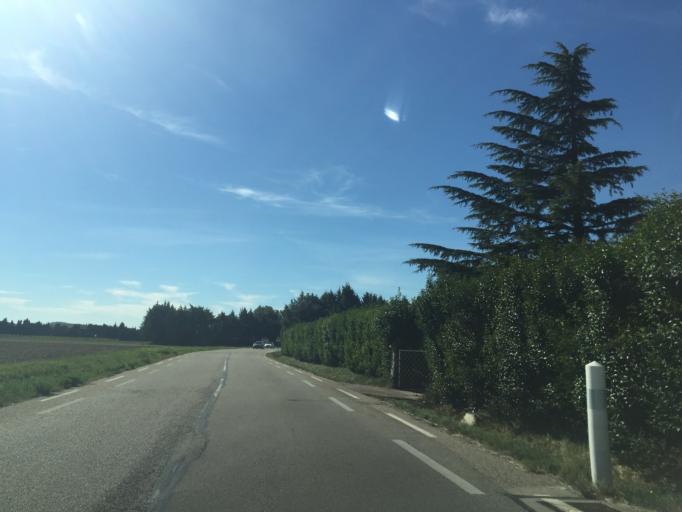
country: FR
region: Provence-Alpes-Cote d'Azur
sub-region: Departement du Vaucluse
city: Caderousse
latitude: 44.1207
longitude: 4.7747
